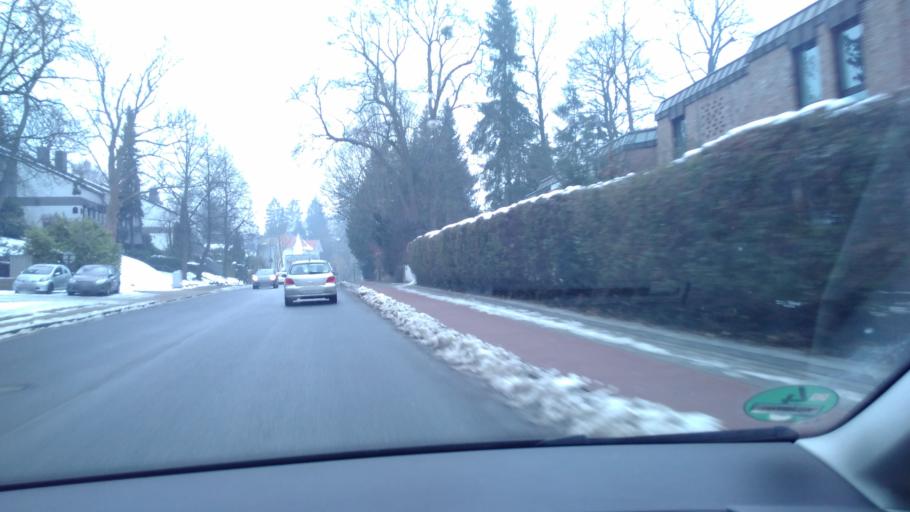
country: DE
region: North Rhine-Westphalia
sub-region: Regierungsbezirk Koln
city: Aachen
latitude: 50.7538
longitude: 6.0691
